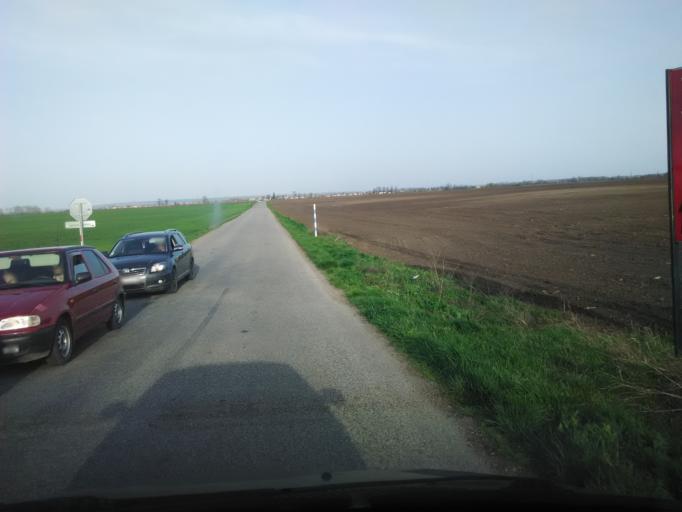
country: SK
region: Nitriansky
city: Surany
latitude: 48.0465
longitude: 18.1502
